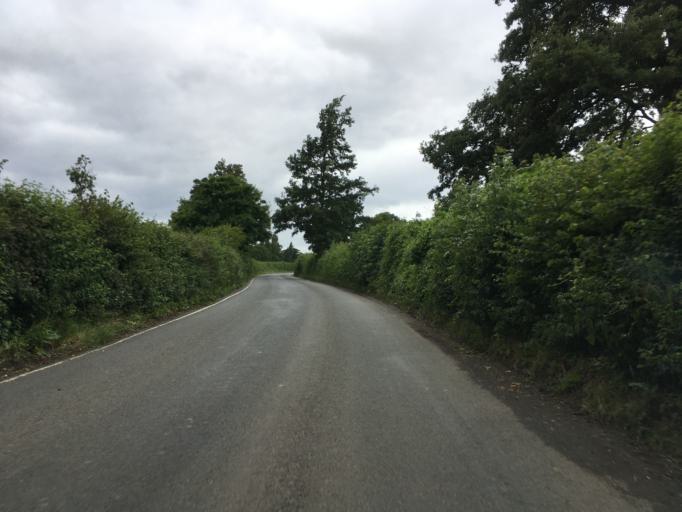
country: GB
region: England
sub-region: Gloucestershire
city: Stonehouse
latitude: 51.7753
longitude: -2.3714
